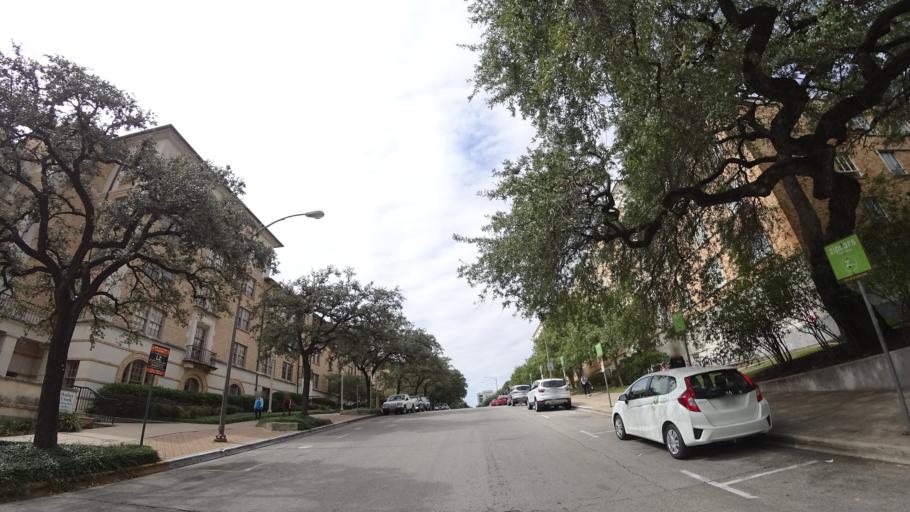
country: US
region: Texas
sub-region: Travis County
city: Austin
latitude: 30.2833
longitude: -97.7348
